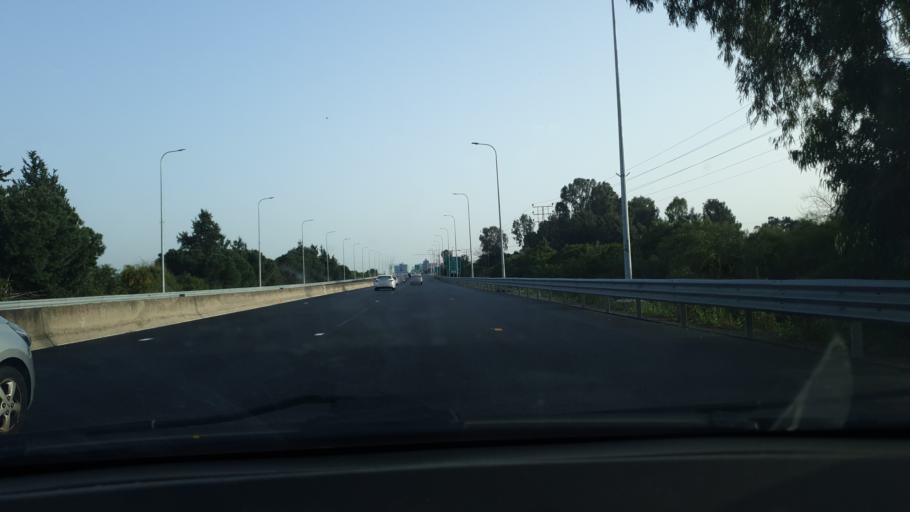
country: IL
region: Central District
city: Ra'anana
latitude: 32.2150
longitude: 34.8835
